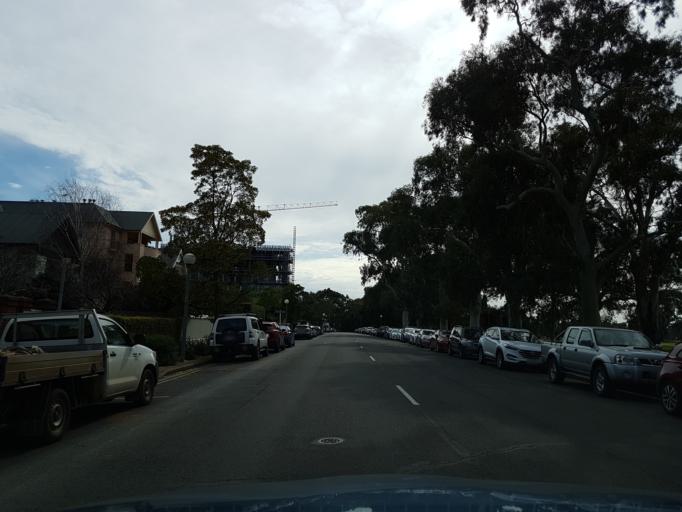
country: AU
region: South Australia
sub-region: Unley
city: Fullarton
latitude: -34.9347
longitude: 138.6179
